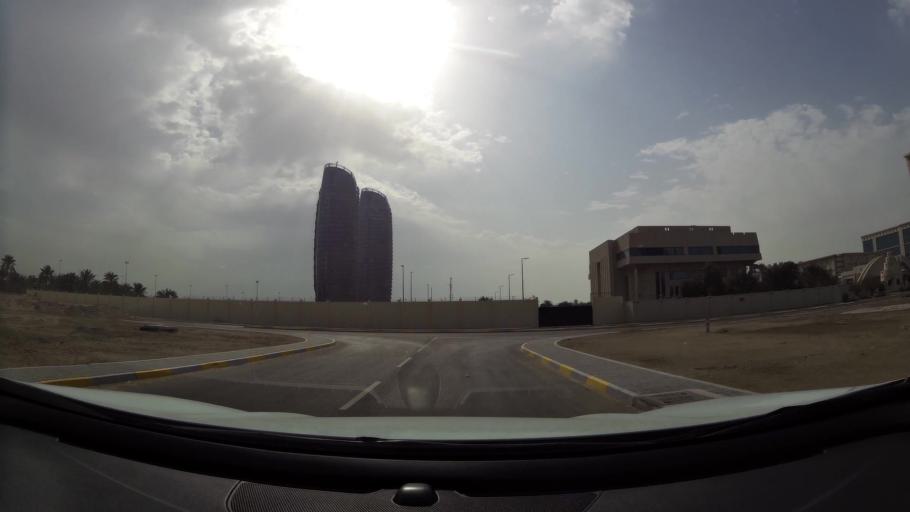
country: AE
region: Abu Dhabi
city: Abu Dhabi
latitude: 24.4582
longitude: 54.3972
